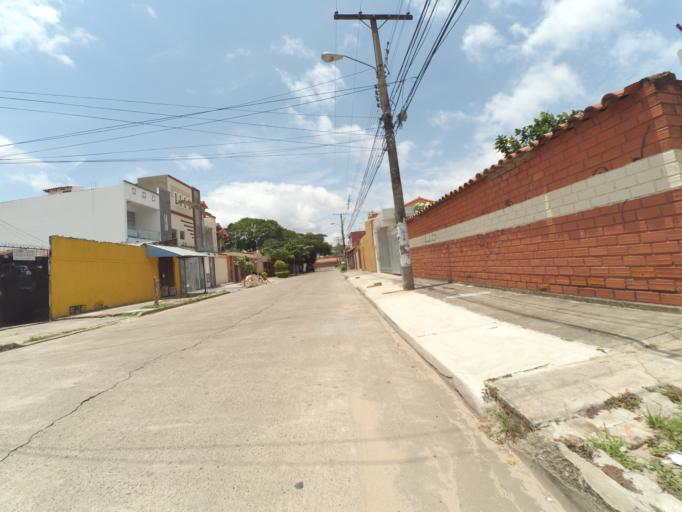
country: BO
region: Santa Cruz
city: Santa Cruz de la Sierra
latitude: -17.7864
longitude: -63.1978
